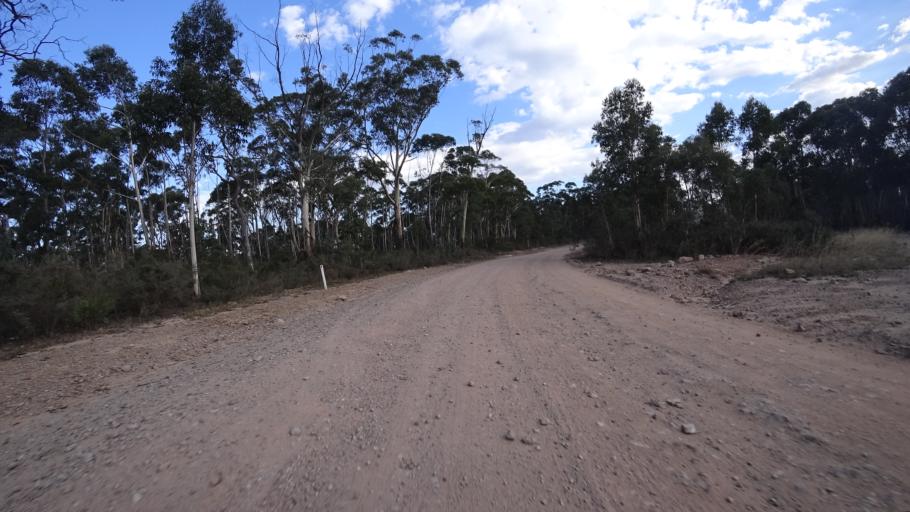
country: AU
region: New South Wales
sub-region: Lithgow
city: Lithgow
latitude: -33.4171
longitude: 150.2047
